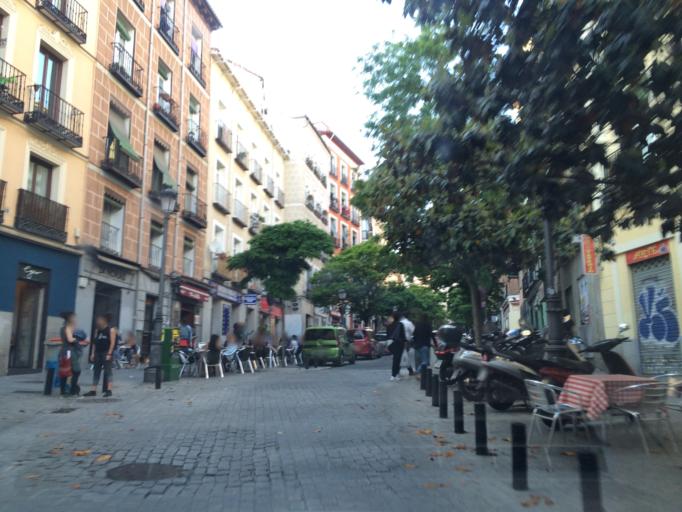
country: ES
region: Madrid
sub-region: Provincia de Madrid
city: Madrid
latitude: 40.4103
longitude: -3.7009
